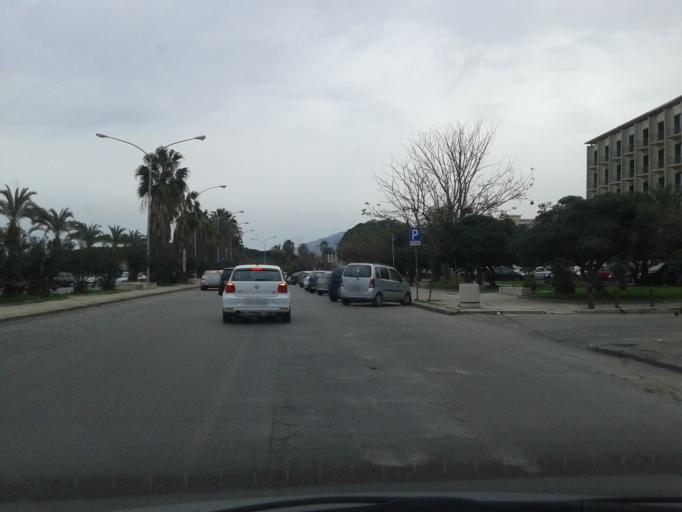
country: IT
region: Sicily
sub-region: Palermo
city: Palermo
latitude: 38.1162
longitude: 13.3746
